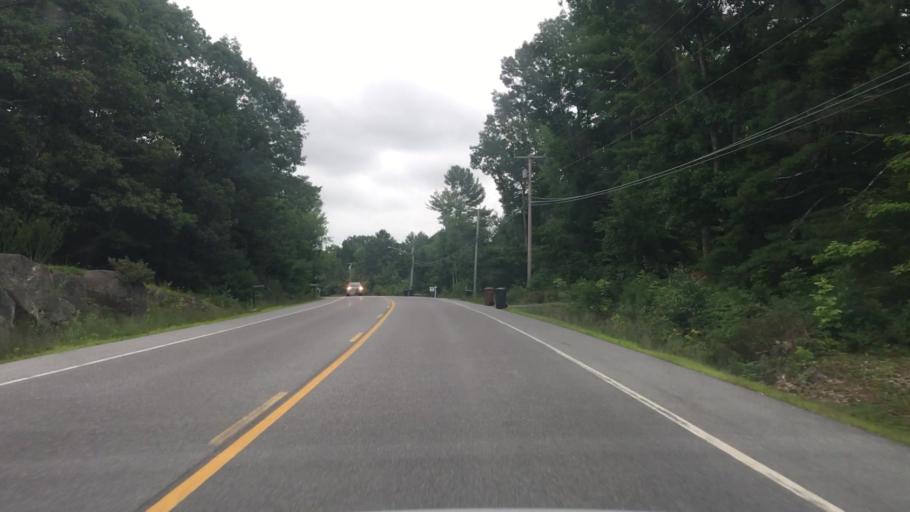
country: US
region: Maine
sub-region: York County
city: Biddeford
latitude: 43.5275
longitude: -70.4999
